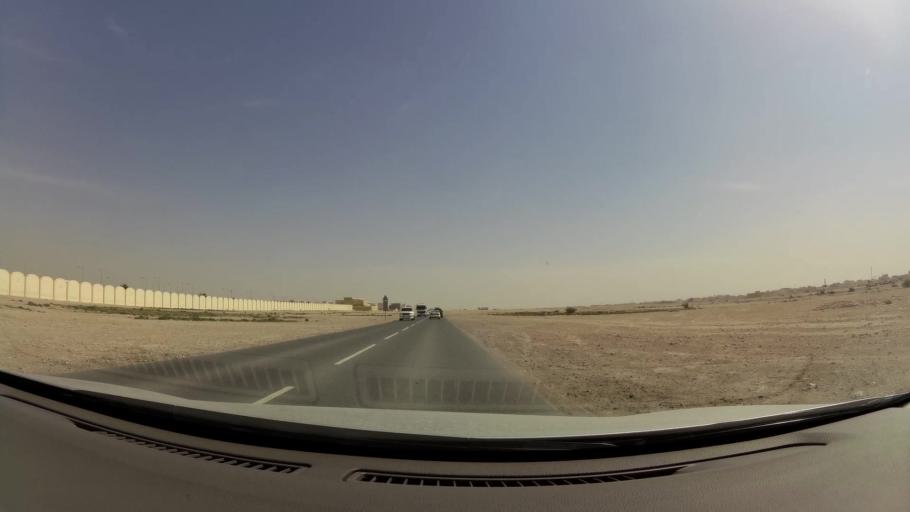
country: QA
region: Baladiyat ar Rayyan
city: Ar Rayyan
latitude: 25.2565
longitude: 51.3837
